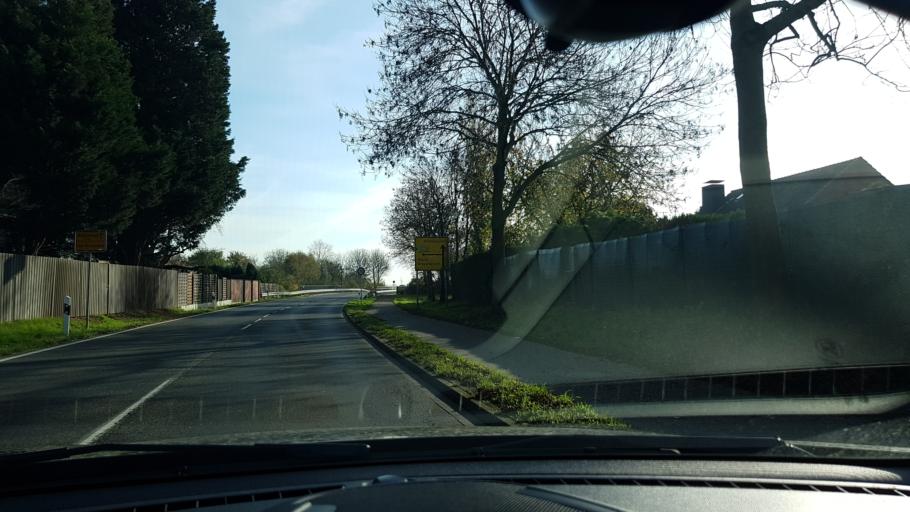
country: DE
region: North Rhine-Westphalia
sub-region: Regierungsbezirk Dusseldorf
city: Neubrueck
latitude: 51.1033
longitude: 6.6249
